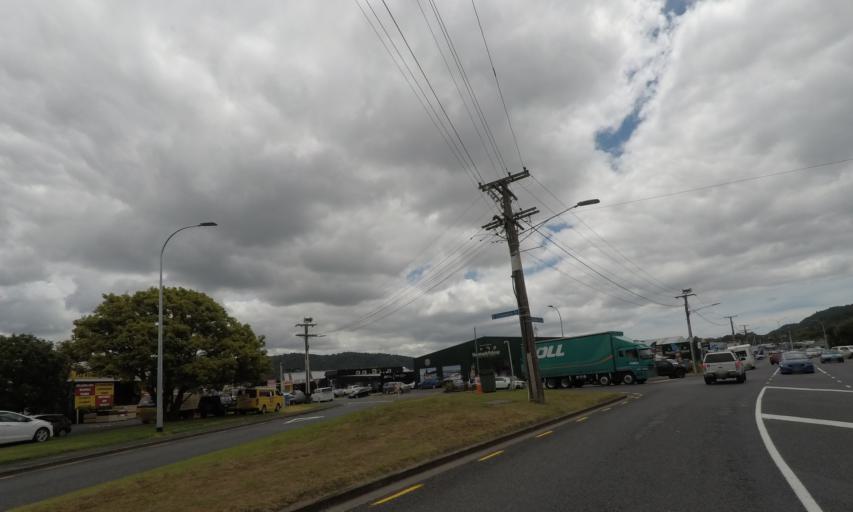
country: NZ
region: Northland
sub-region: Whangarei
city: Whangarei
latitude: -35.7316
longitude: 174.3265
